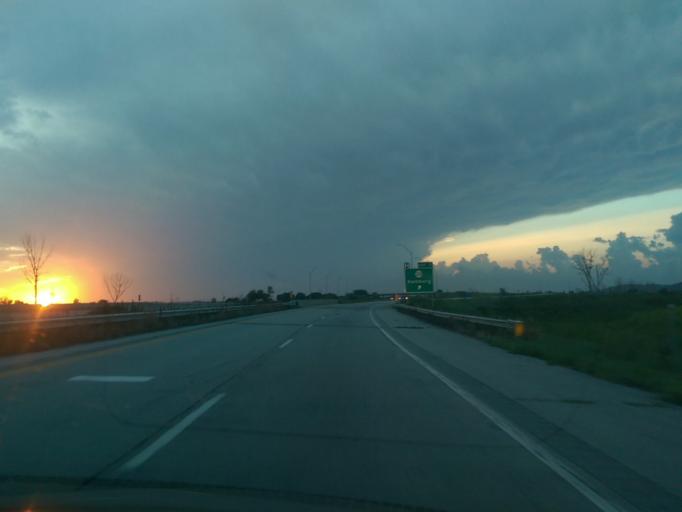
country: US
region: Iowa
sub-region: Fremont County
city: Hamburg
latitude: 40.5947
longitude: -95.6719
